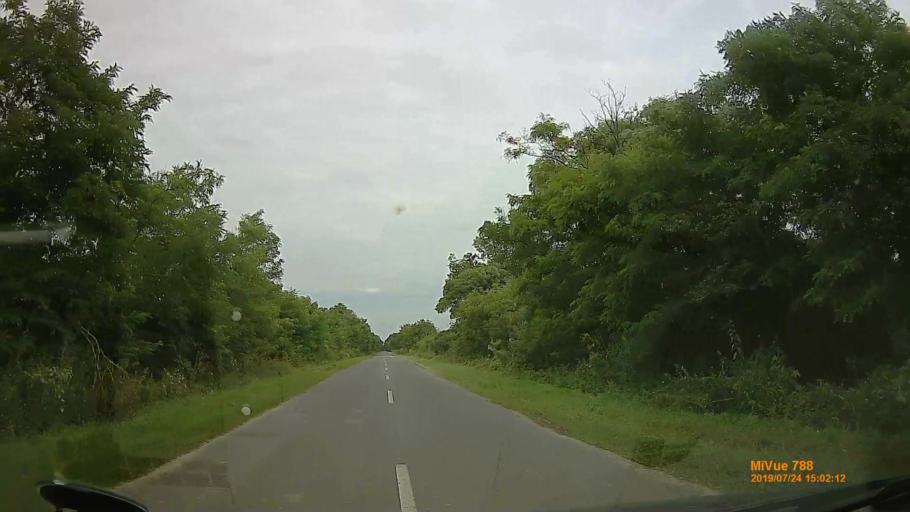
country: HU
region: Szabolcs-Szatmar-Bereg
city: Vasarosnameny
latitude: 48.2258
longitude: 22.4023
